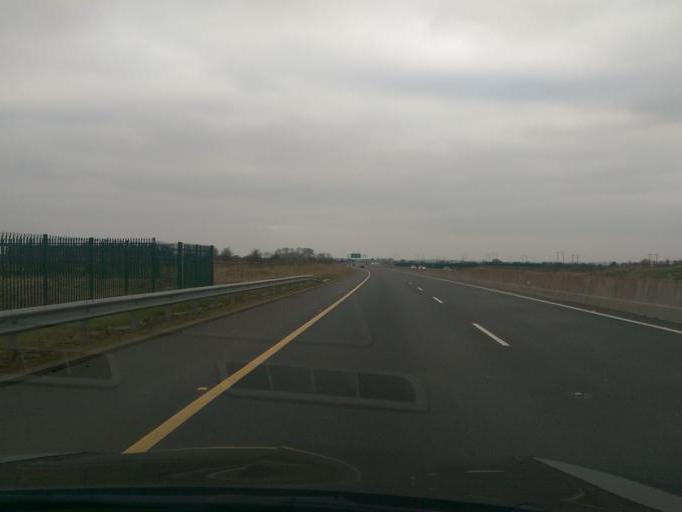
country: IE
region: Connaught
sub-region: County Galway
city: Oranmore
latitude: 53.2986
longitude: -8.8909
